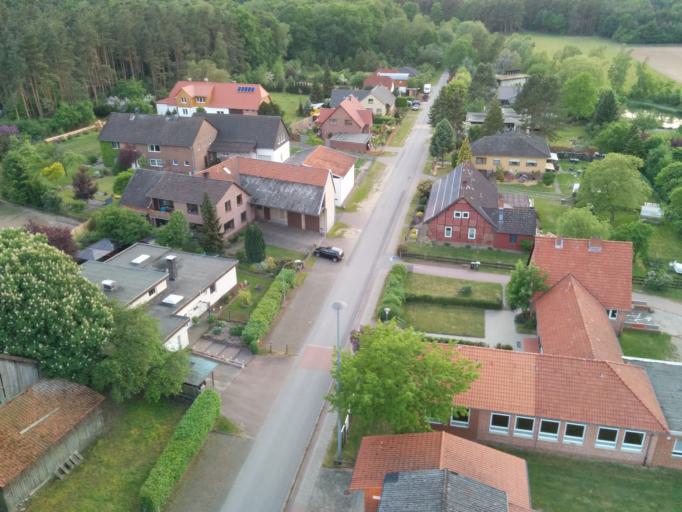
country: DE
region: Lower Saxony
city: Hillerse
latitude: 52.4451
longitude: 10.3837
